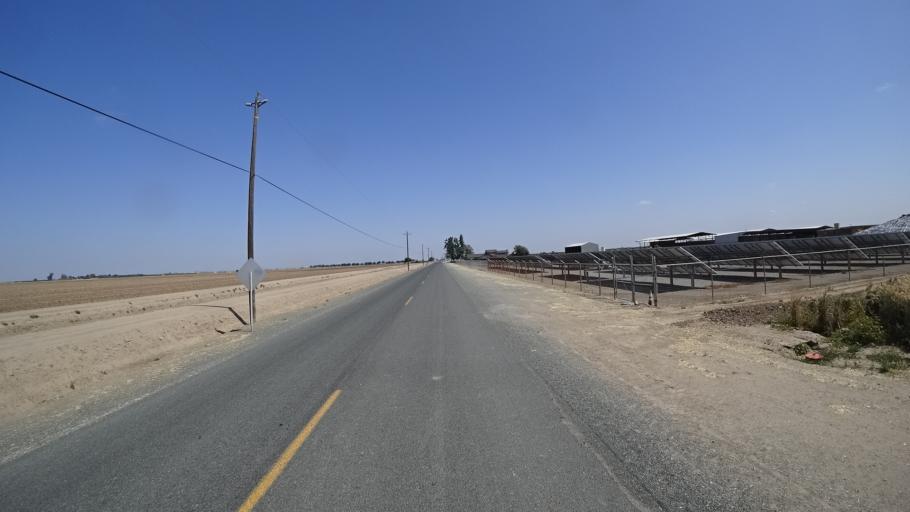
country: US
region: California
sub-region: Kings County
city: Home Garden
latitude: 36.2271
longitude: -119.6189
